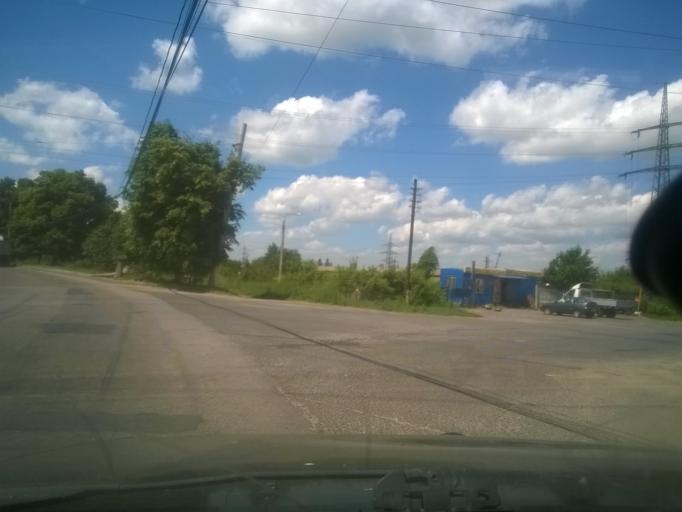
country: RU
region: Kursk
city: Voroshnevo
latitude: 51.6667
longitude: 36.1157
